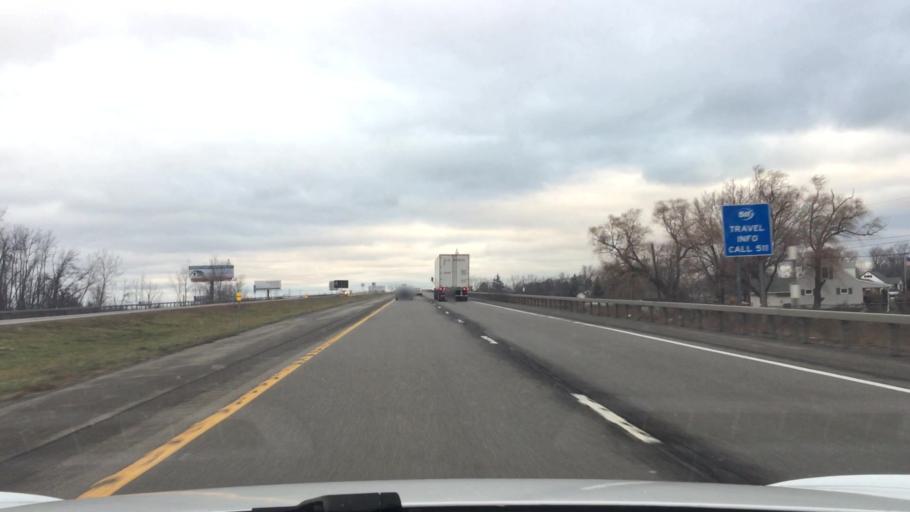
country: US
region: New York
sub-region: Niagara County
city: Niagara Falls
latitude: 43.1130
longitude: -78.9972
